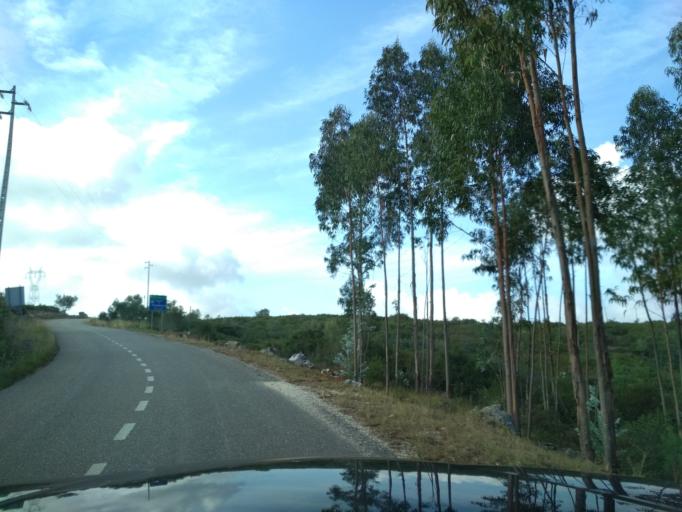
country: PT
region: Coimbra
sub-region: Condeixa-A-Nova
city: Condeixa-a-Nova
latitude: 40.0837
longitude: -8.5061
